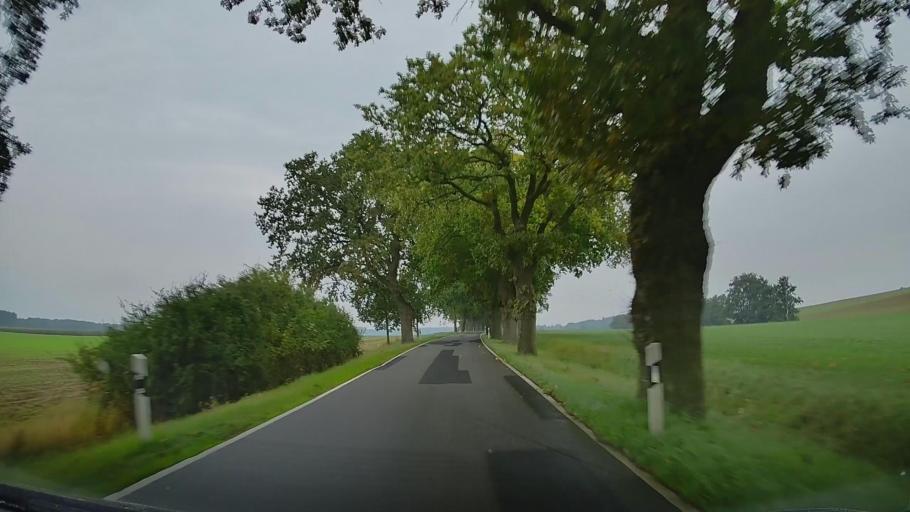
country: DE
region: Mecklenburg-Vorpommern
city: Kalkhorst
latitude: 53.9867
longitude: 11.0442
